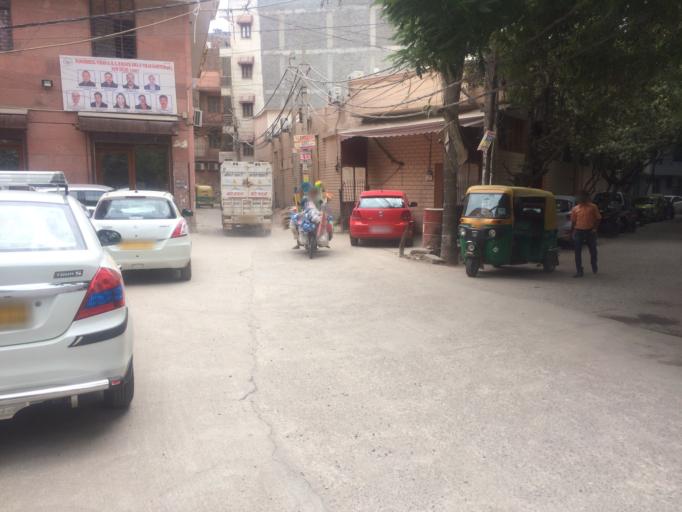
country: IN
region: NCT
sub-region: New Delhi
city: New Delhi
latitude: 28.5359
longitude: 77.2227
